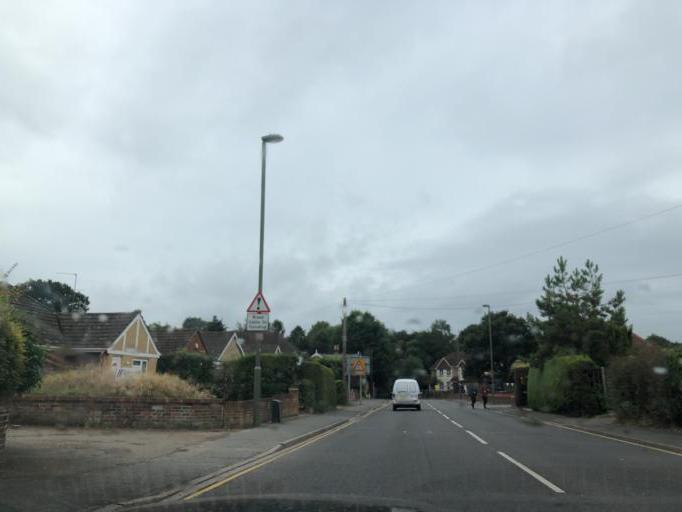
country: GB
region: England
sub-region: Surrey
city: Frimley
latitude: 51.3012
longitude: -0.7278
